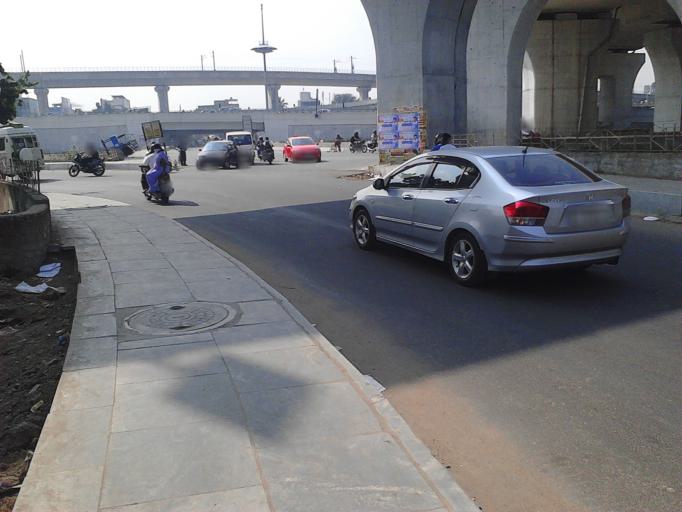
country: IN
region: Tamil Nadu
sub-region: Kancheepuram
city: Alandur
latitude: 13.0087
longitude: 80.2040
